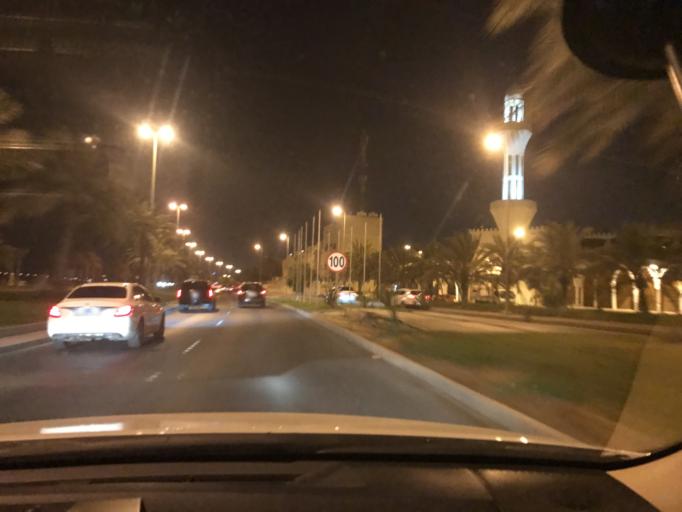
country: BH
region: Muharraq
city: Al Muharraq
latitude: 26.2550
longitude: 50.6217
